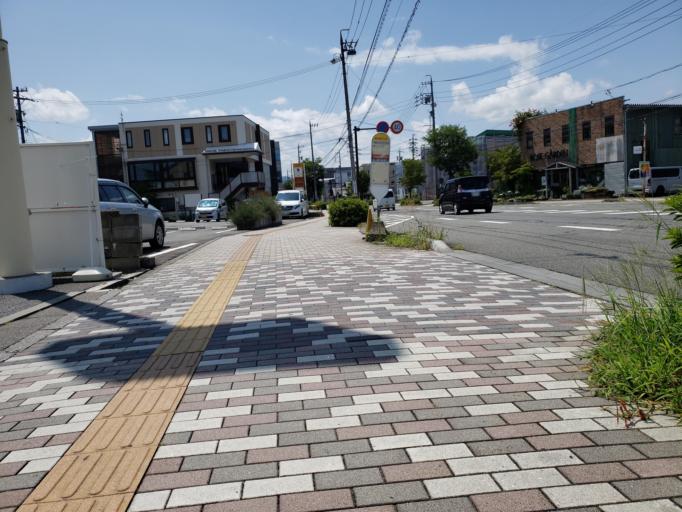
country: JP
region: Nagano
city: Nagano-shi
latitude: 36.6365
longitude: 138.1913
